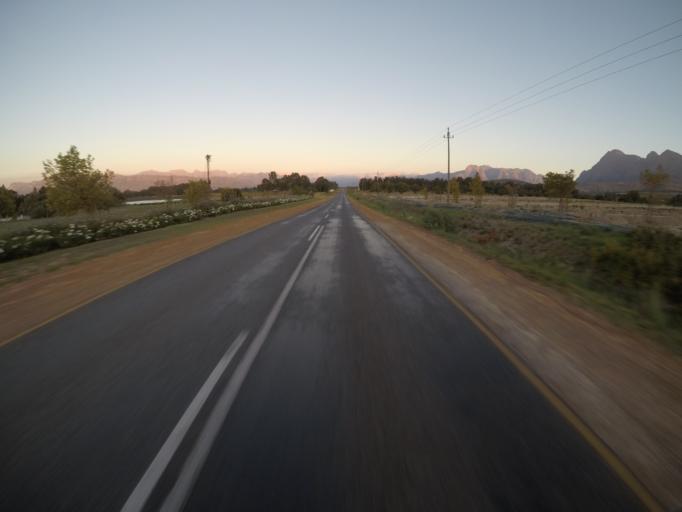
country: ZA
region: Western Cape
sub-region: Cape Winelands District Municipality
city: Paarl
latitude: -33.8141
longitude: 18.9142
